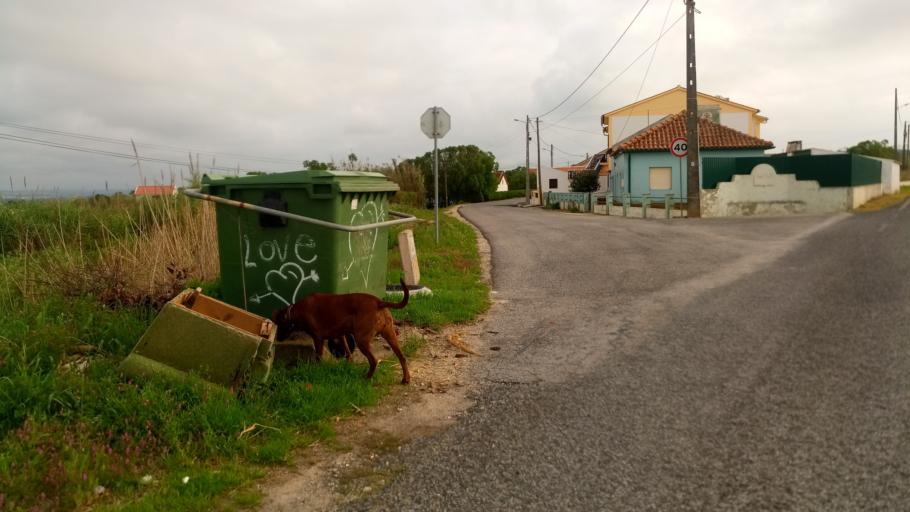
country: PT
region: Leiria
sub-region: Caldas da Rainha
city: Caldas da Rainha
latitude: 39.4810
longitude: -9.1845
